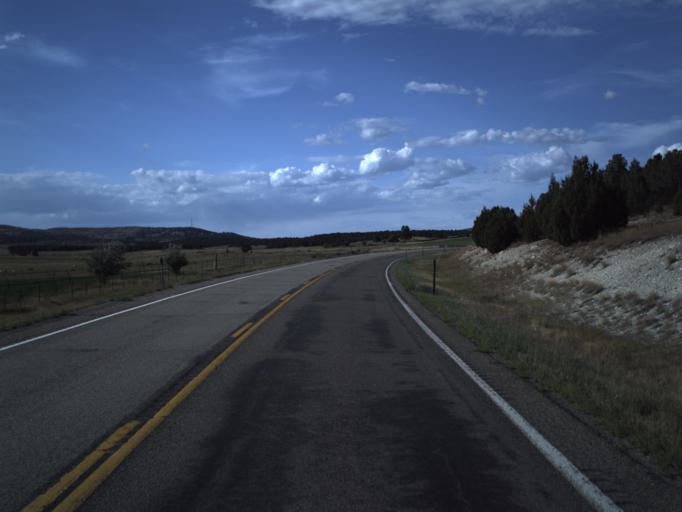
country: US
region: Utah
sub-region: Sanpete County
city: Fairview
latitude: 39.6474
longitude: -111.4508
